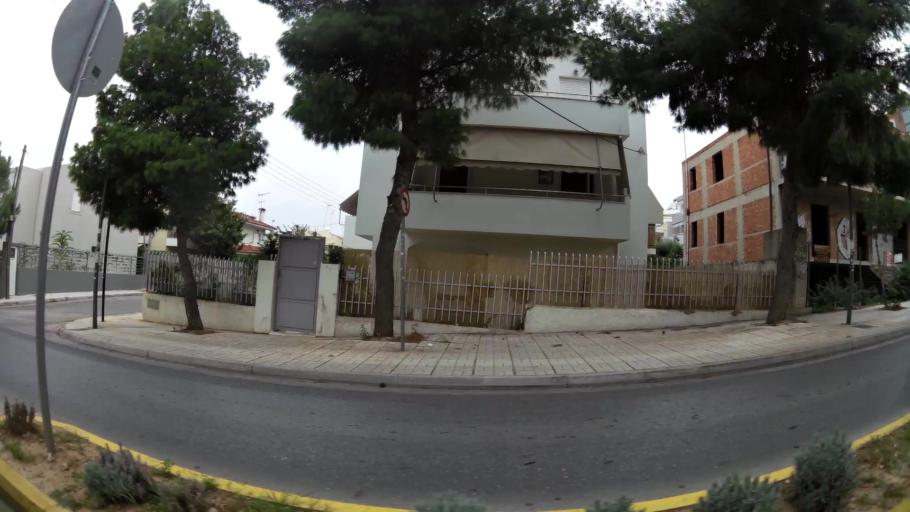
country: GR
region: Attica
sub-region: Nomarchia Athinas
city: Alimos
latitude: 37.9082
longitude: 23.7335
